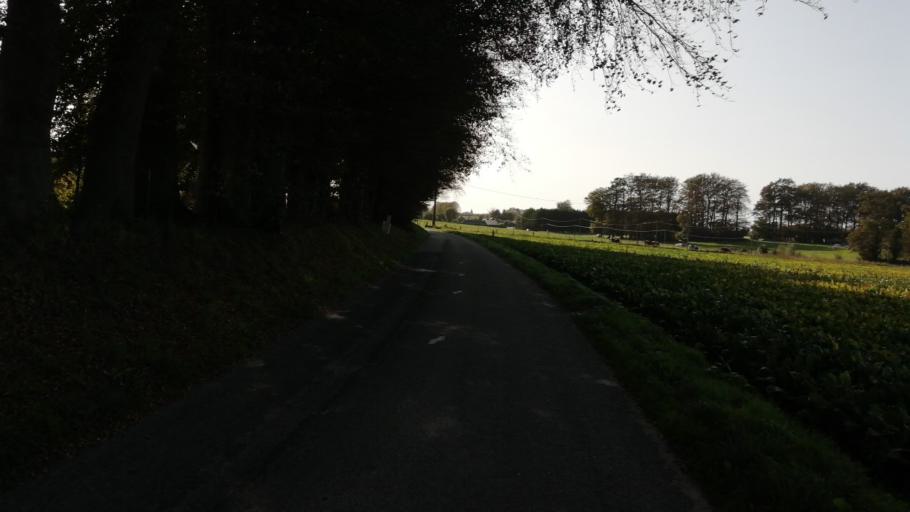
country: FR
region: Haute-Normandie
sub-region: Departement de la Seine-Maritime
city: Etainhus
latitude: 49.5897
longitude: 0.3011
